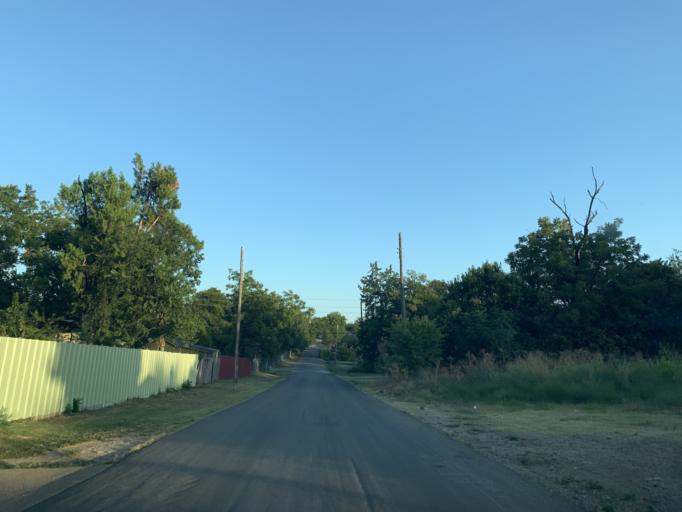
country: US
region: Texas
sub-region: Dallas County
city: Dallas
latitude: 32.7005
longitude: -96.8074
